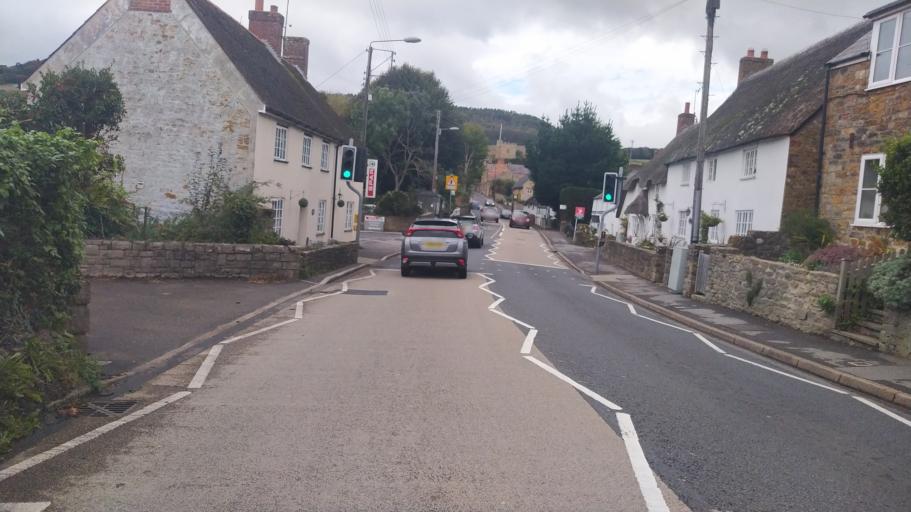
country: GB
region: England
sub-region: Dorset
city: Bridport
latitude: 50.7320
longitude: -2.8182
